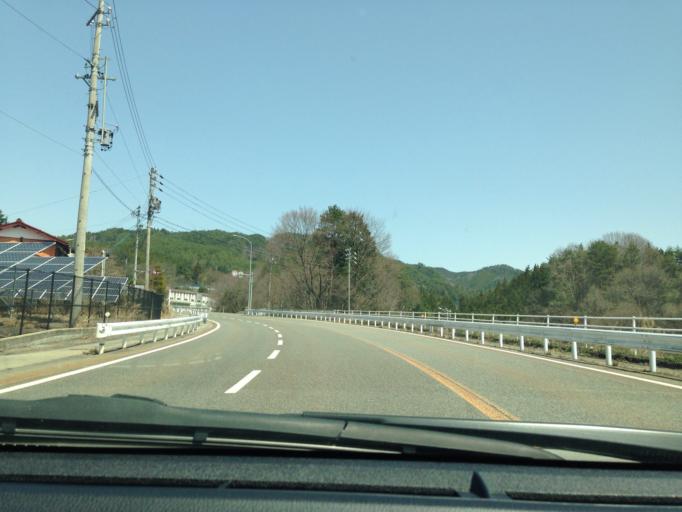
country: JP
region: Gifu
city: Takayama
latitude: 36.0746
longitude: 137.2679
